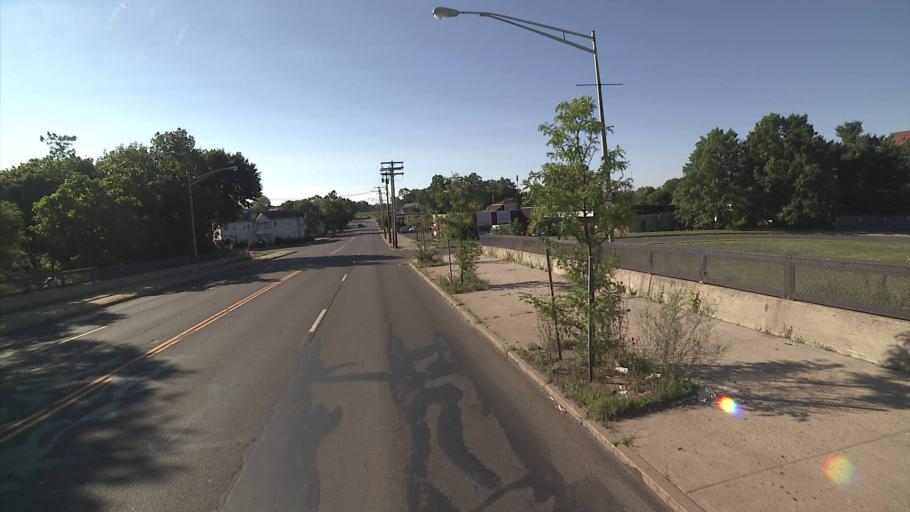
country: US
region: Connecticut
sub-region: New Haven County
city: West Haven
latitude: 41.2878
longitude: -72.9379
